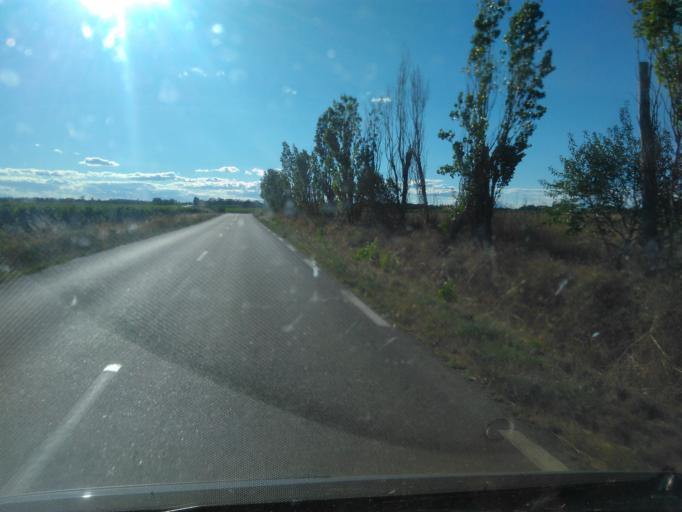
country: FR
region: Languedoc-Roussillon
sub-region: Departement du Gard
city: Vauvert
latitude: 43.6513
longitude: 4.3117
